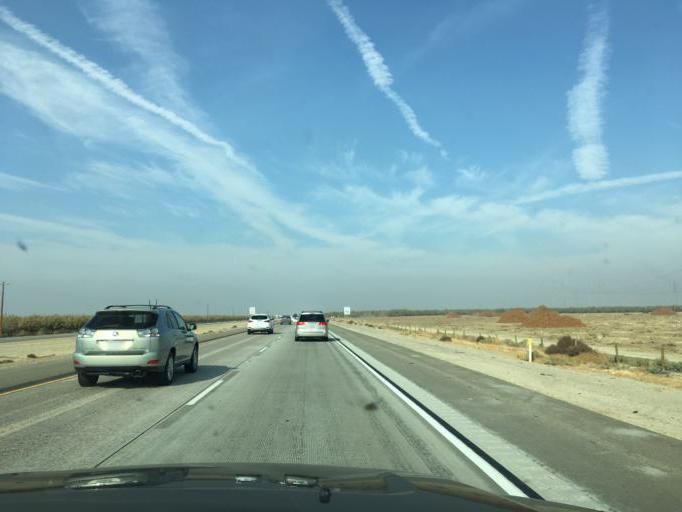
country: US
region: California
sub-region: Kern County
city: Buttonwillow
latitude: 35.5074
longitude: -119.5426
